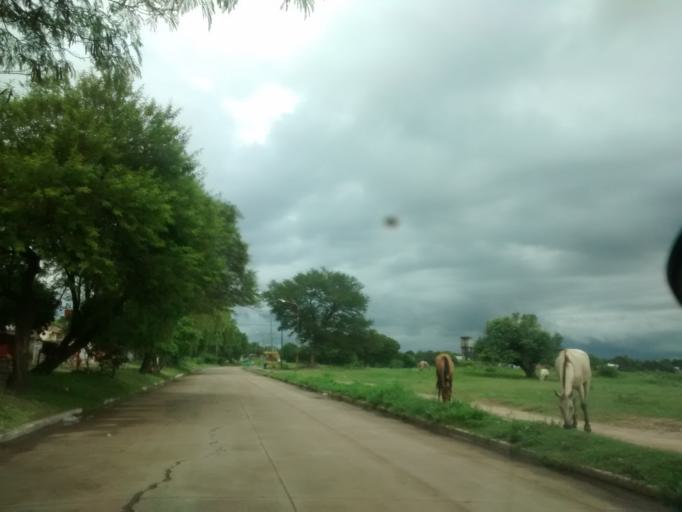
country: AR
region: Chaco
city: Puerto Tirol
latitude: -27.3796
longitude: -59.0894
